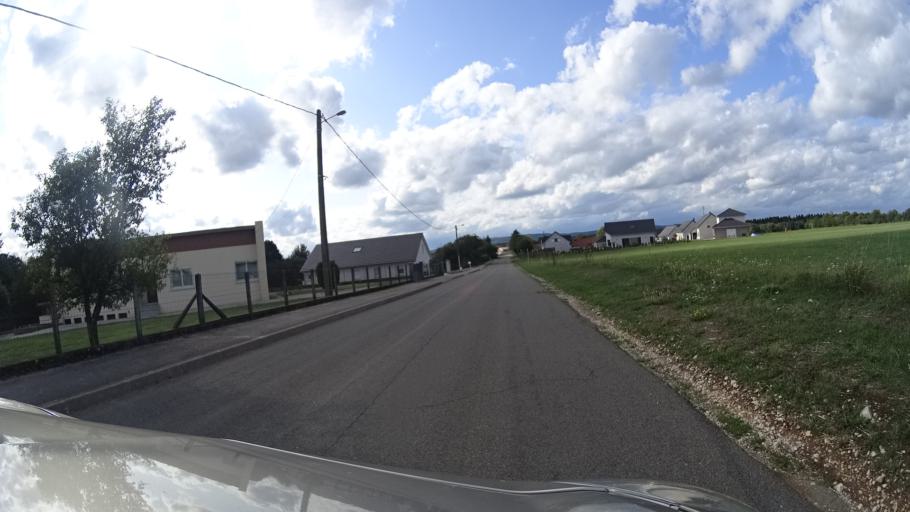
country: FR
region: Franche-Comte
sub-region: Departement du Doubs
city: Mamirolle
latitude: 47.2035
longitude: 6.1543
